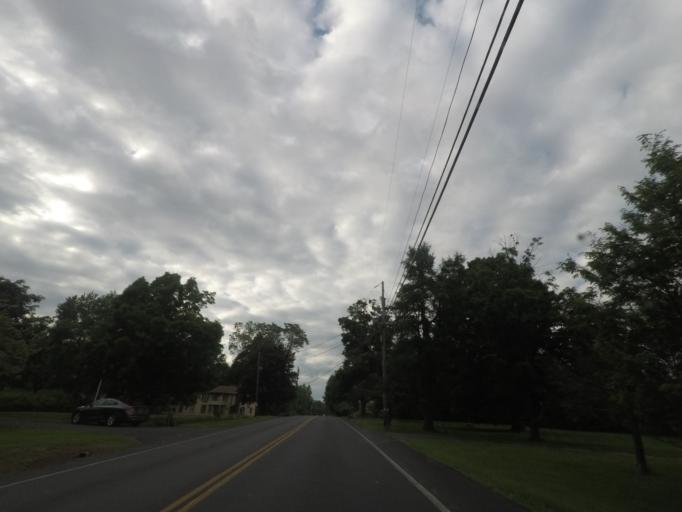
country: US
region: New York
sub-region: Orange County
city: Orange Lake
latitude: 41.5822
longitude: -74.1164
